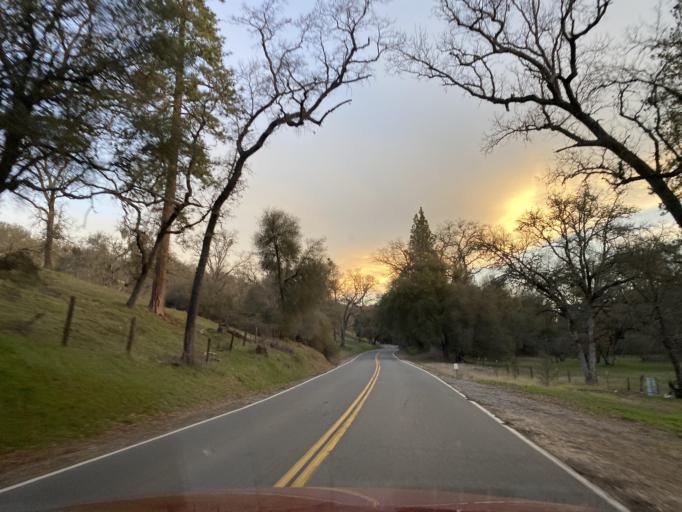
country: US
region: California
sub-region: Amador County
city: Plymouth
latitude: 38.4962
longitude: -120.7889
